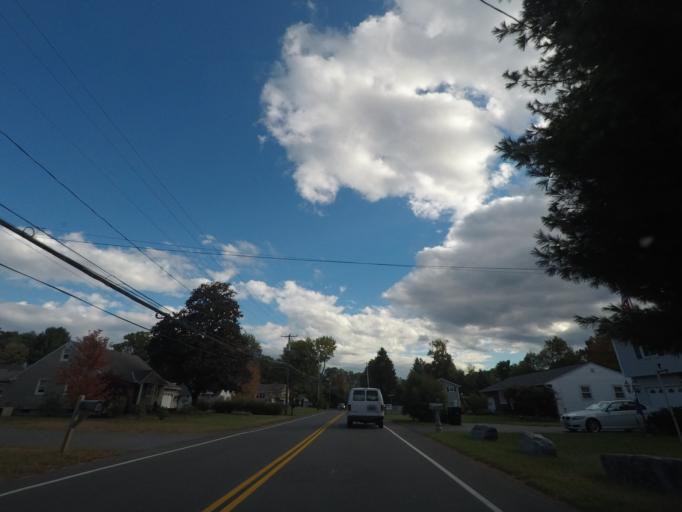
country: US
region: New York
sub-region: Schenectady County
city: Niskayuna
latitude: 42.7501
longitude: -73.8385
